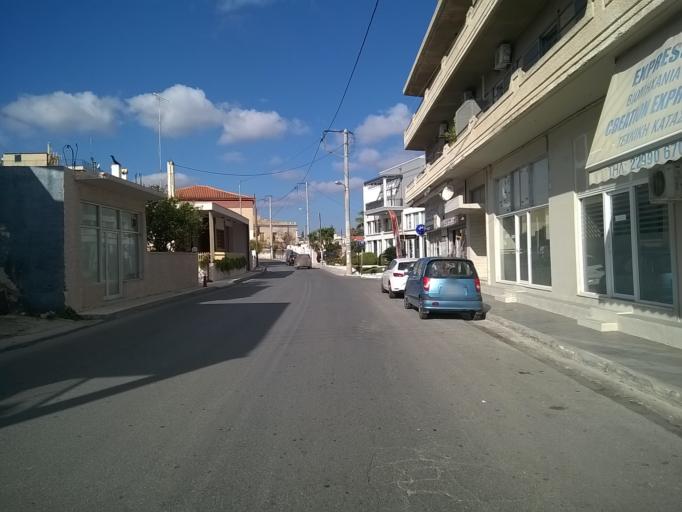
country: GR
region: Attica
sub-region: Nomarchia Anatolikis Attikis
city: Keratea
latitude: 37.8077
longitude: 23.9808
